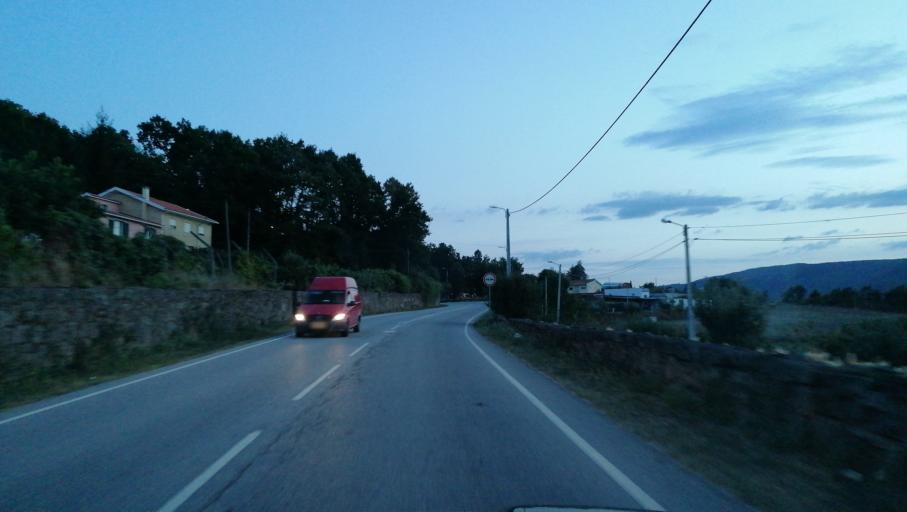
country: PT
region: Vila Real
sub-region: Vila Pouca de Aguiar
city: Vila Pouca de Aguiar
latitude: 41.5359
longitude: -7.6080
